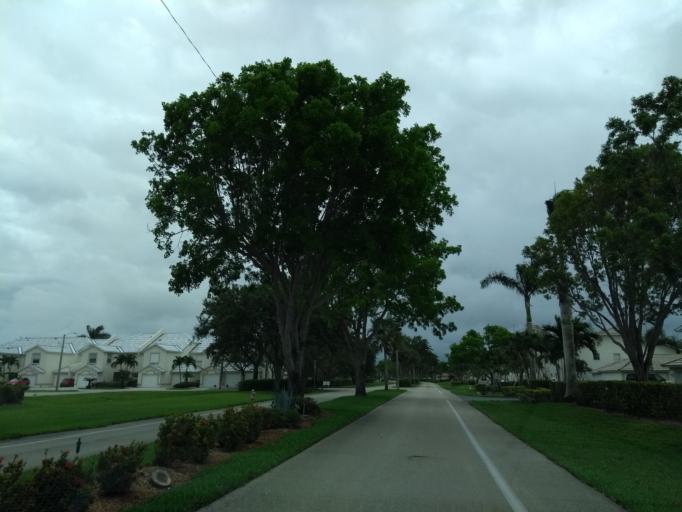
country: US
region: Florida
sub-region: Collier County
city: Marco
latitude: 25.9553
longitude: -81.5124
